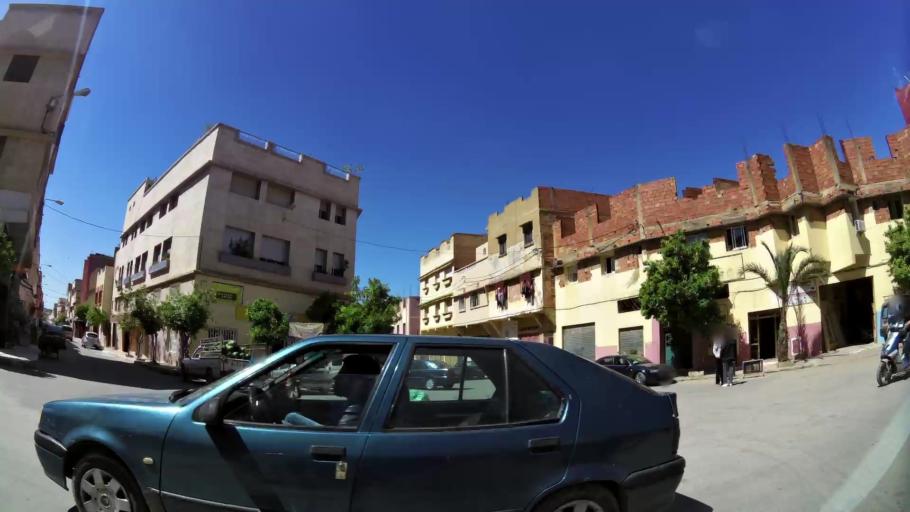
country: MA
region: Meknes-Tafilalet
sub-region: Meknes
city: Meknes
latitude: 33.8667
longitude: -5.5511
